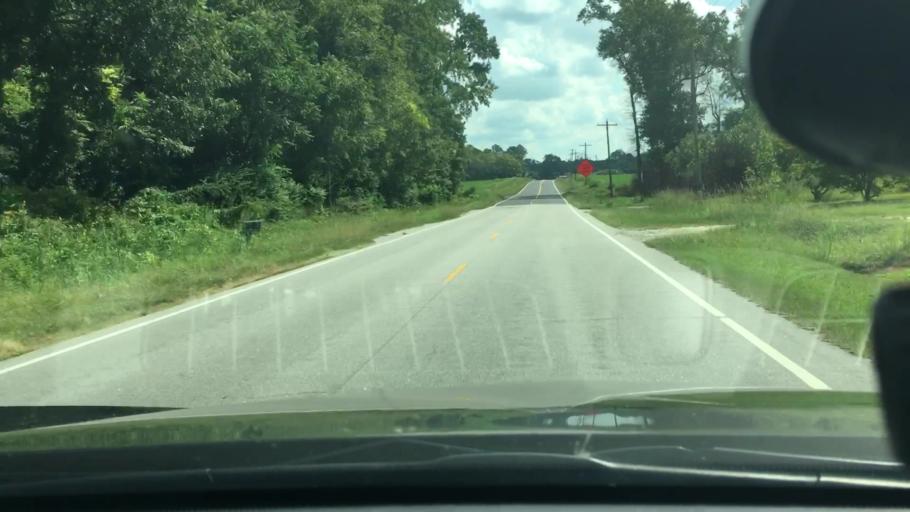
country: US
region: North Carolina
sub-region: Edgecombe County
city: Pinetops
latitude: 35.7791
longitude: -77.5907
